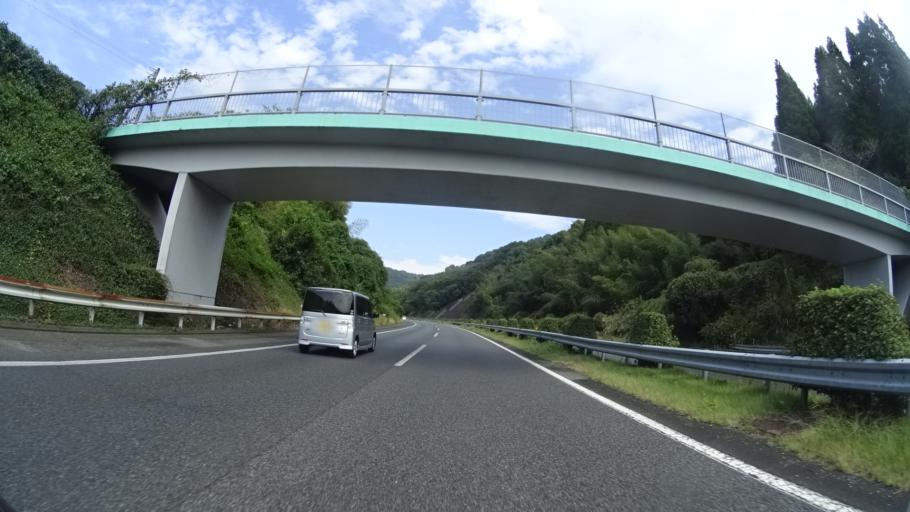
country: JP
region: Kumamoto
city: Matsubase
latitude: 32.6075
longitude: 130.7233
